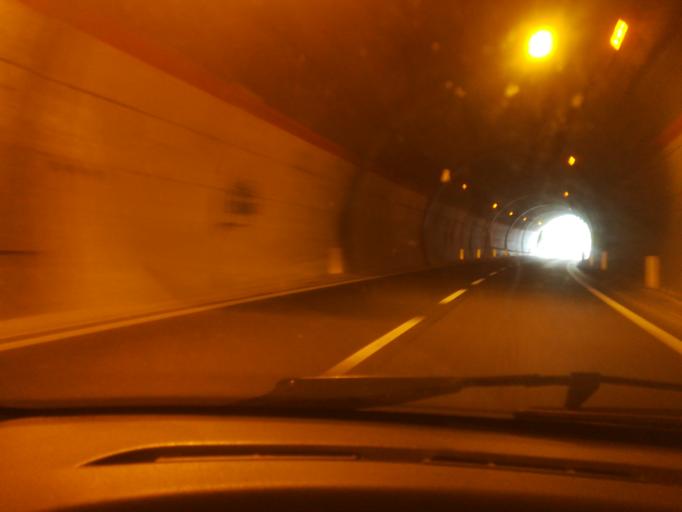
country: IT
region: The Marches
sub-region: Provincia di Macerata
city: Belforte del Chienti
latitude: 43.1631
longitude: 13.2463
